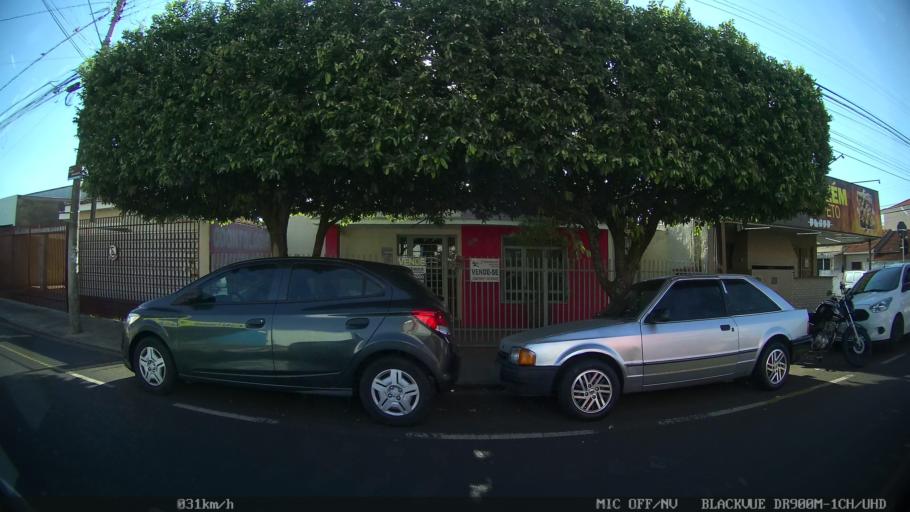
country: BR
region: Sao Paulo
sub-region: Sao Jose Do Rio Preto
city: Sao Jose do Rio Preto
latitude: -20.7943
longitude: -49.3642
